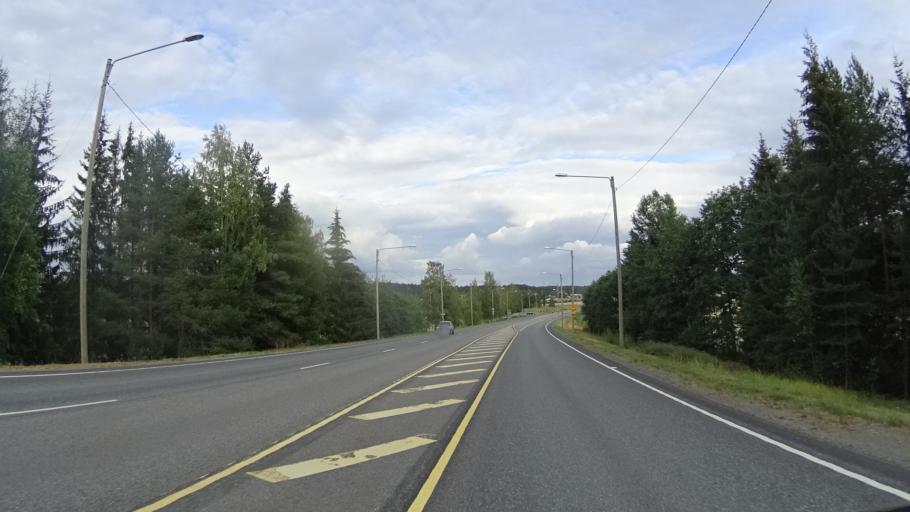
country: FI
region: Haeme
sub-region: Haemeenlinna
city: Parola
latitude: 61.0252
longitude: 24.3198
